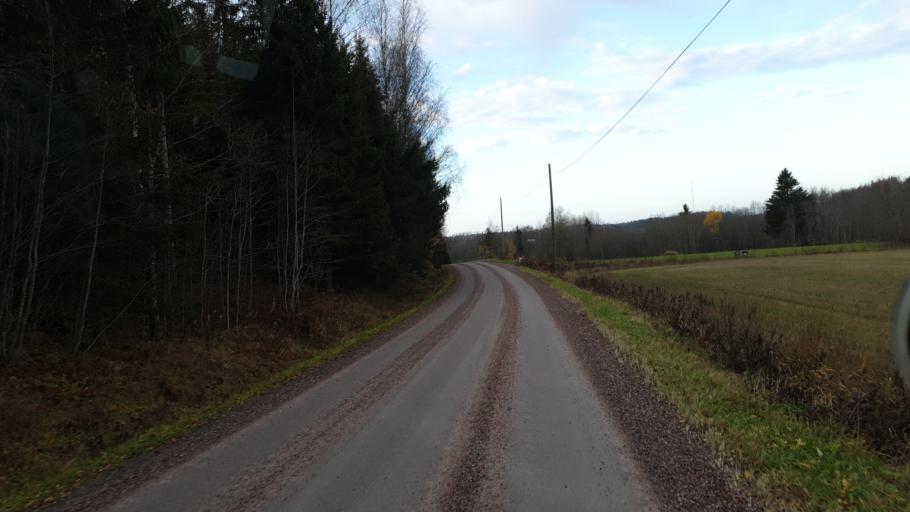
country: FI
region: Uusimaa
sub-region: Helsinki
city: Siuntio
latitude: 60.1457
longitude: 24.2651
